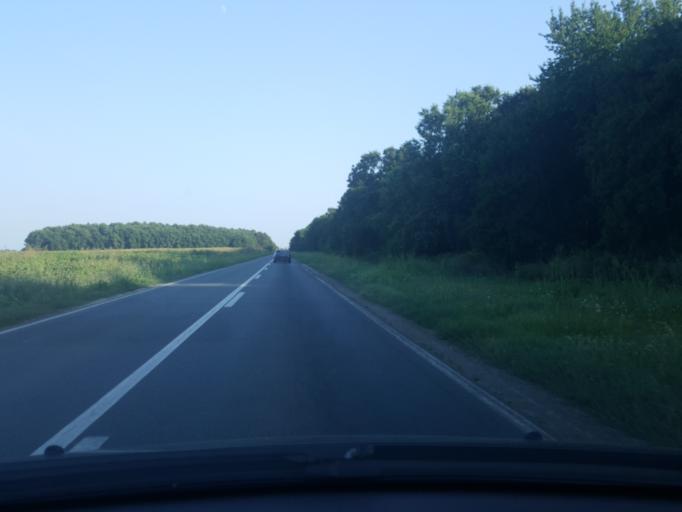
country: RS
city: Platicevo
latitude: 44.8426
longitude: 19.7674
